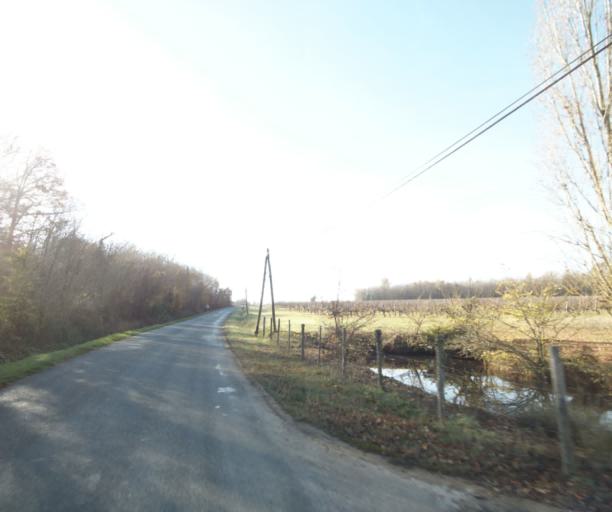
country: FR
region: Poitou-Charentes
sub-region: Departement de la Charente-Maritime
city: Cherac
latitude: 45.7284
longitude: -0.4530
